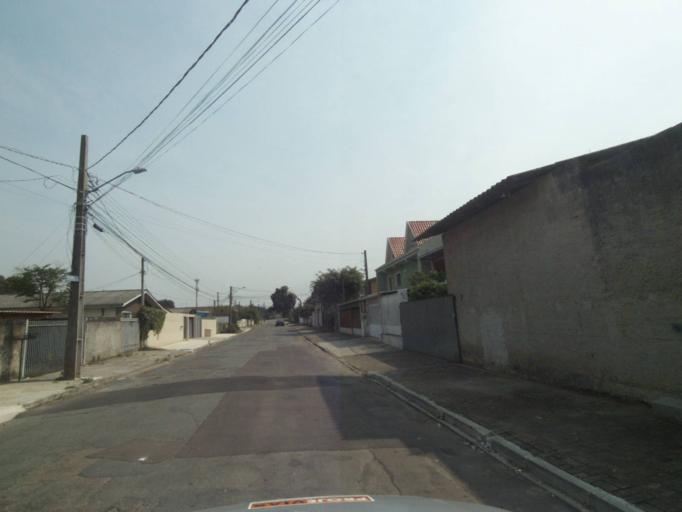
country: BR
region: Parana
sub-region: Pinhais
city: Pinhais
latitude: -25.4757
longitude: -49.2246
